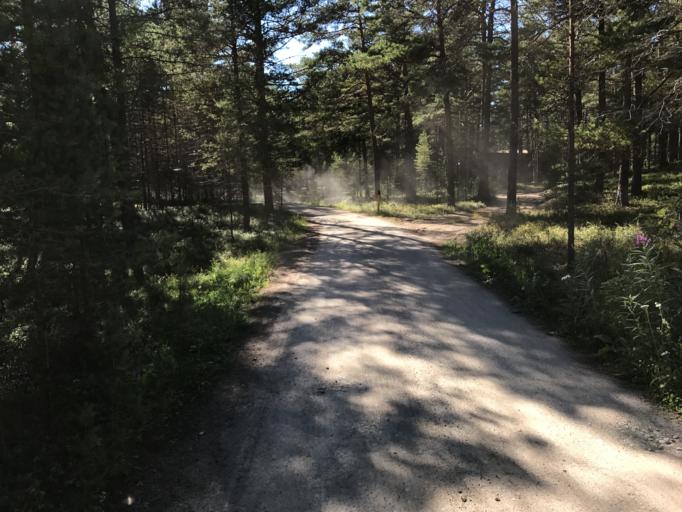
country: EE
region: Harju
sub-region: Paldiski linn
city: Paldiski
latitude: 59.3856
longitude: 24.2252
